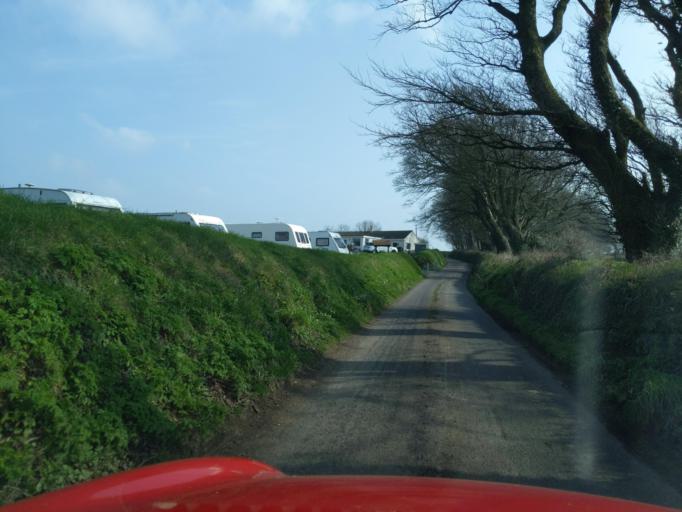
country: GB
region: England
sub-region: Devon
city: Kingsbridge
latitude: 50.3100
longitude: -3.7708
